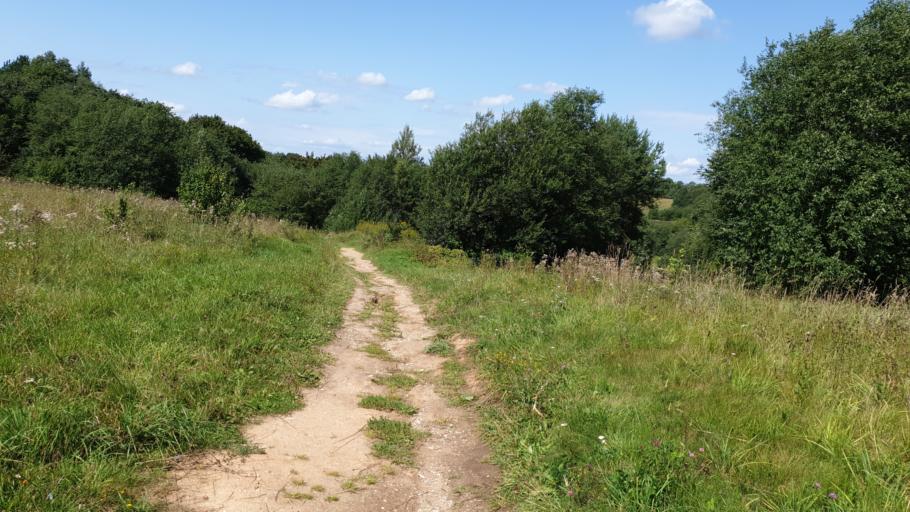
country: LT
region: Vilnius County
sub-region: Vilniaus Rajonas
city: Vievis
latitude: 54.8228
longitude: 24.9456
